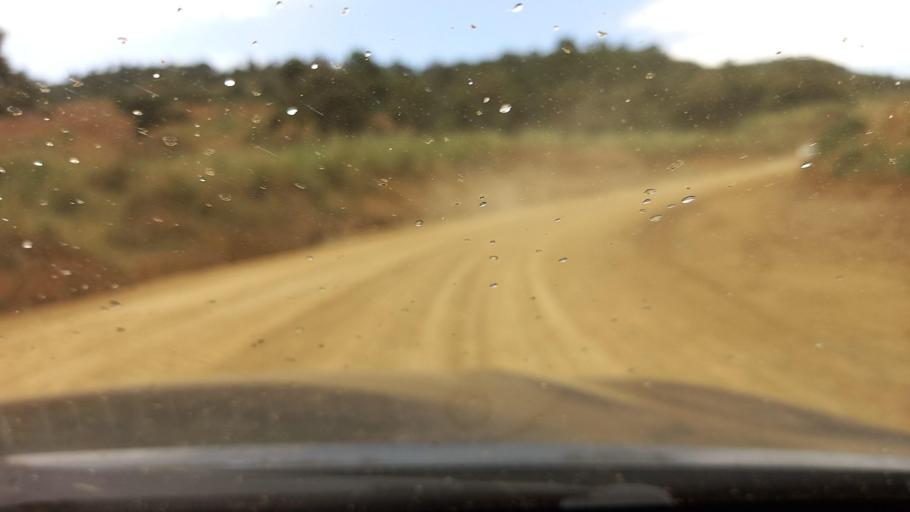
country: ET
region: Southern Nations, Nationalities, and People's Region
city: Mizan Teferi
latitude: 6.2001
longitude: 35.6600
